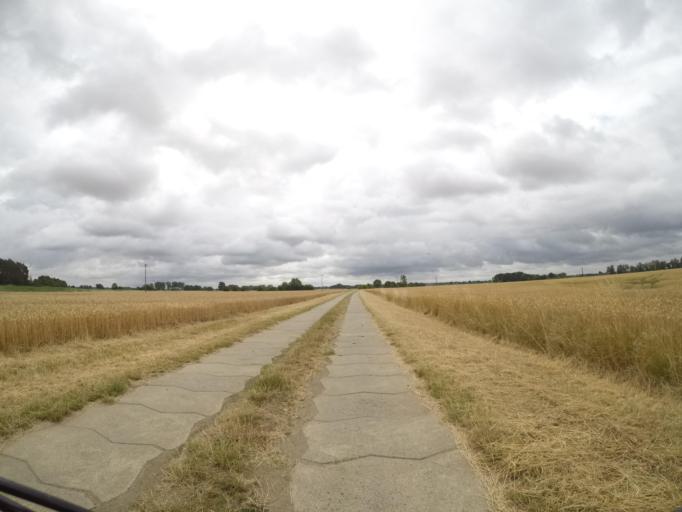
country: DE
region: Lower Saxony
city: Damnatz
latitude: 53.1822
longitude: 11.1164
